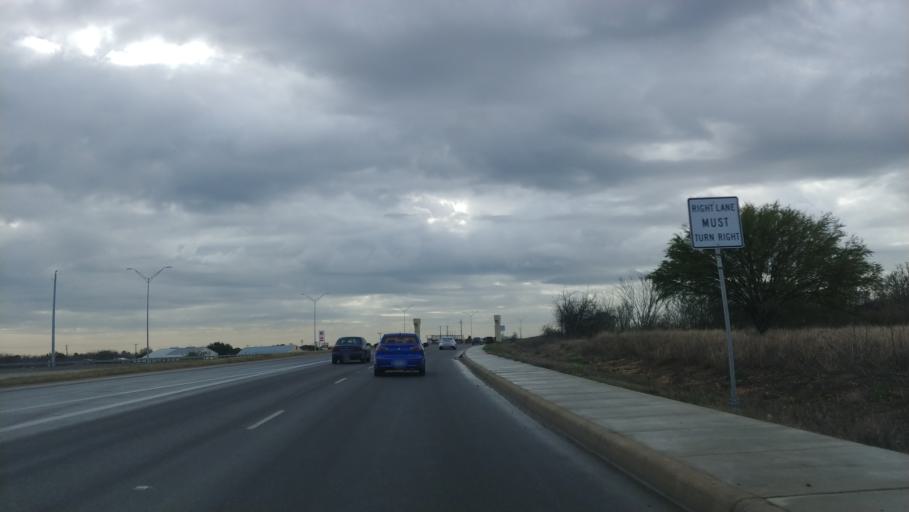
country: US
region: Texas
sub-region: Bexar County
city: Lackland Air Force Base
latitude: 29.3983
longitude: -98.7043
